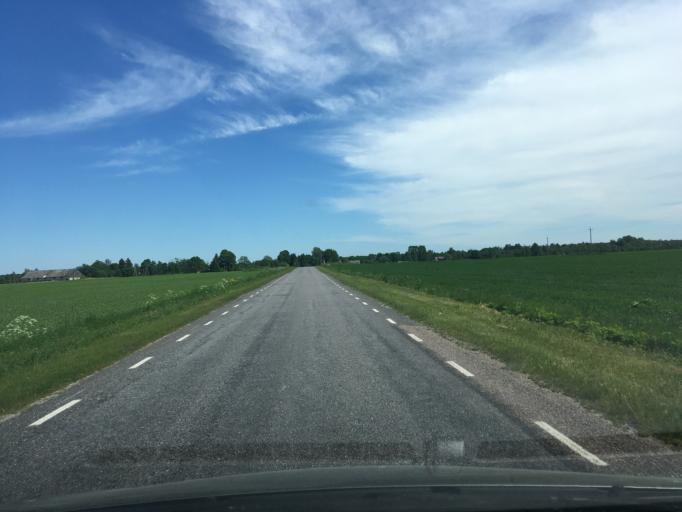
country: EE
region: Raplamaa
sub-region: Rapla vald
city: Rapla
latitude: 59.0448
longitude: 24.8706
